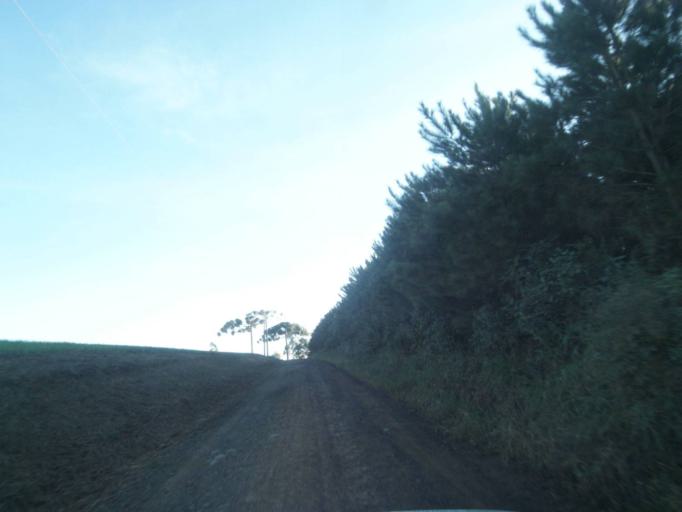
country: BR
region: Parana
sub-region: Telemaco Borba
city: Telemaco Borba
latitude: -24.4326
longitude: -50.6006
